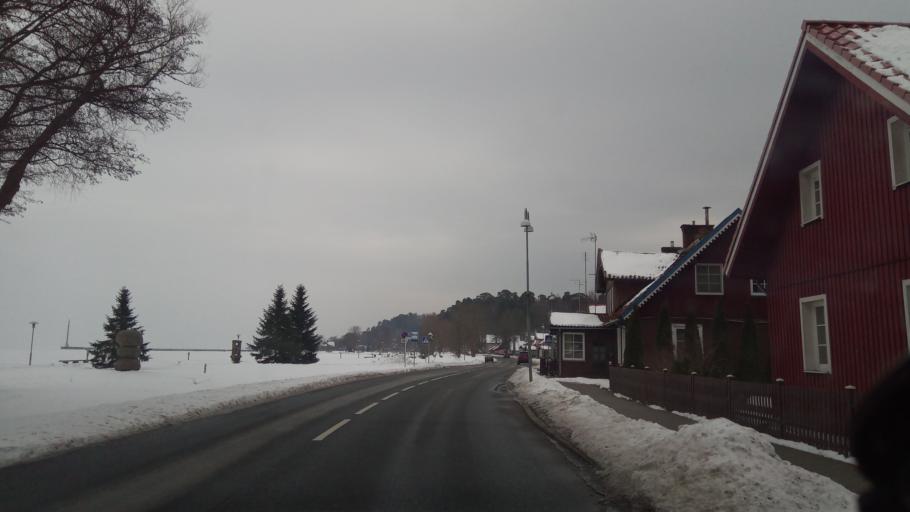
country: LT
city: Neringa
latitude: 55.5390
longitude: 21.1193
